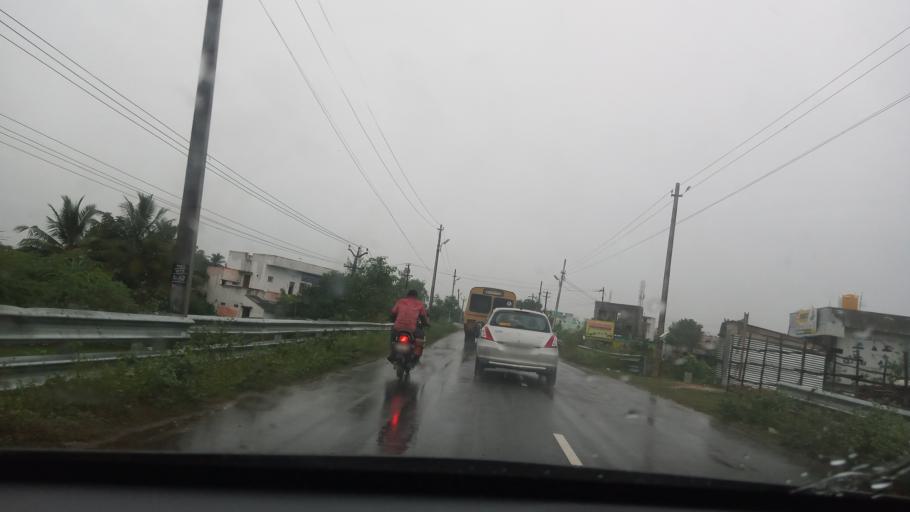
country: IN
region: Tamil Nadu
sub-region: Tiruvannamalai
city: Cheyyar
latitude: 12.6670
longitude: 79.5366
